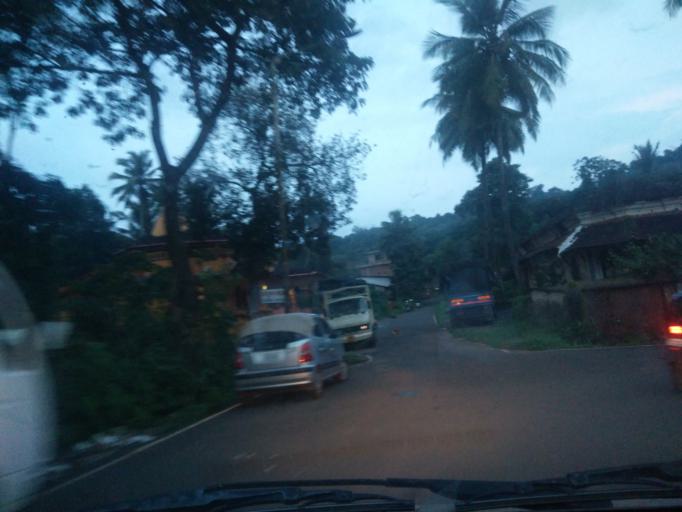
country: IN
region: Goa
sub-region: South Goa
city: Madgaon
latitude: 15.2744
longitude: 73.9637
